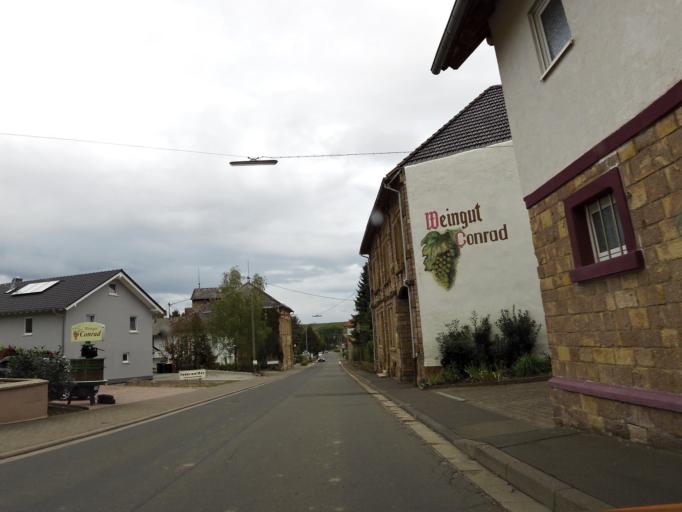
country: DE
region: Rheinland-Pfalz
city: Volxheim
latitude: 49.8168
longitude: 7.9255
